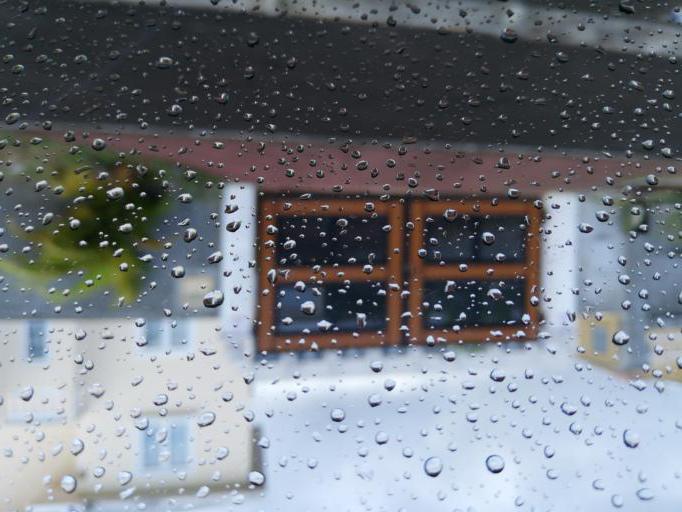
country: MU
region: Plaines Wilhems
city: Ebene
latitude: -20.2451
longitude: 57.4824
